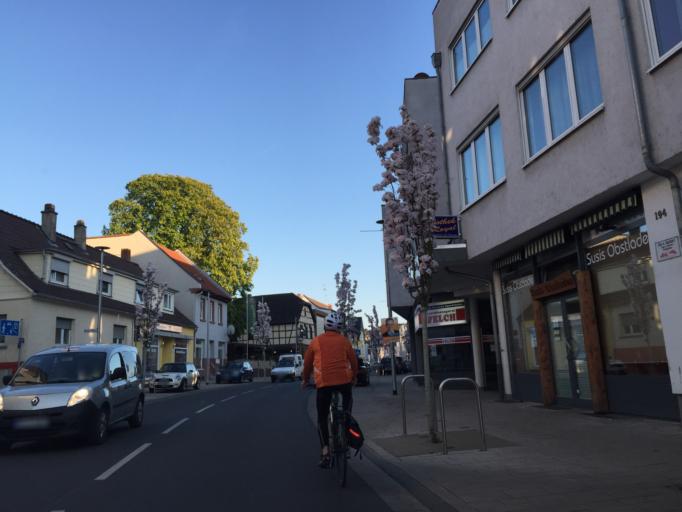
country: DE
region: Hesse
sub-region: Regierungsbezirk Darmstadt
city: Bensheim
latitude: 49.7024
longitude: 8.6200
